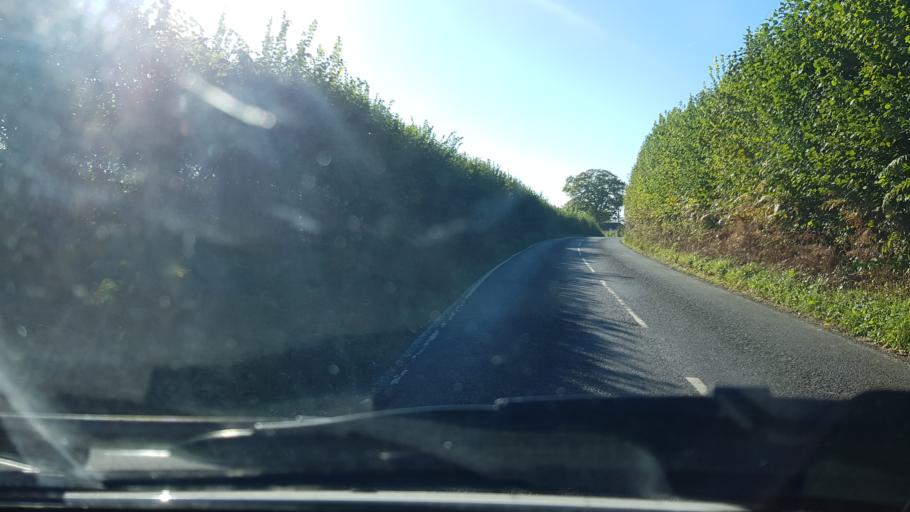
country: GB
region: England
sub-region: Surrey
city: Cranleigh
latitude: 51.1558
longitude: -0.4899
